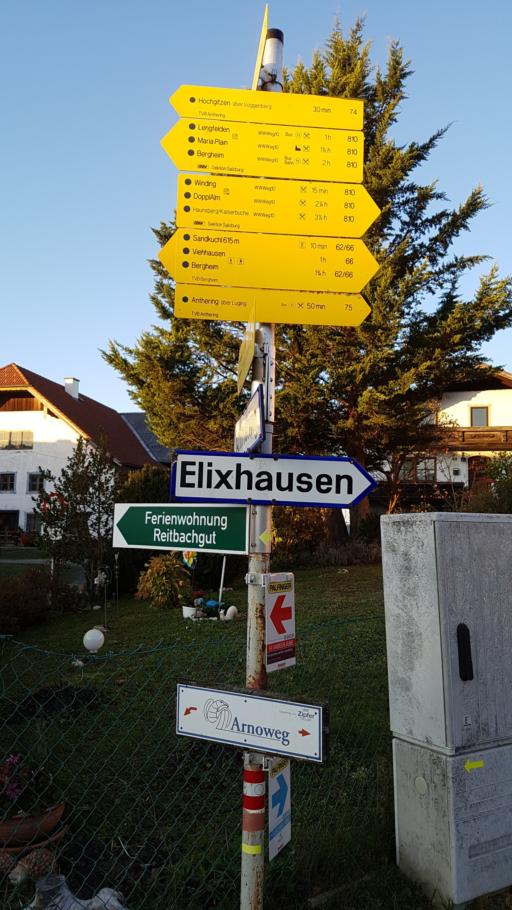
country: AT
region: Salzburg
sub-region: Politischer Bezirk Salzburg-Umgebung
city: Anthering
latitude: 47.8667
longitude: 13.0329
